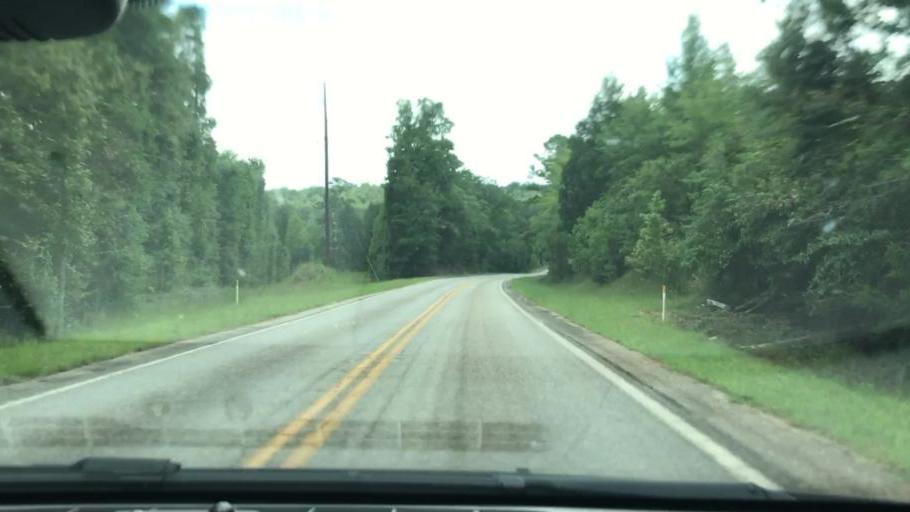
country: US
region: Georgia
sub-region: Stewart County
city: Lumpkin
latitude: 32.0582
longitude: -84.8153
